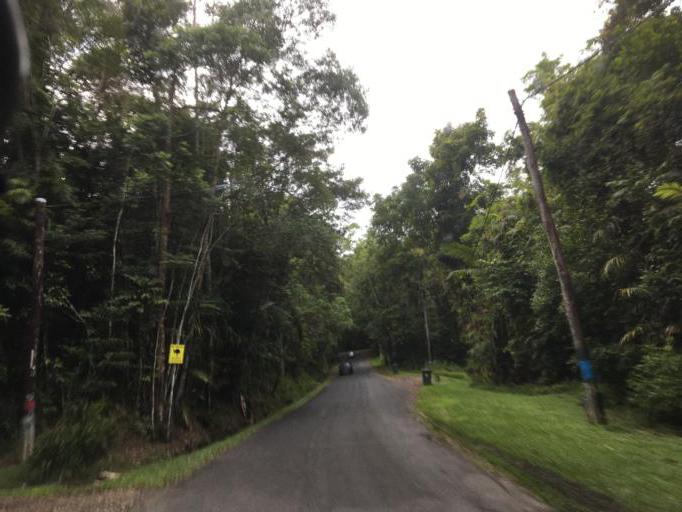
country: AU
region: Queensland
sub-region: Tablelands
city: Kuranda
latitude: -16.8336
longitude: 145.6349
